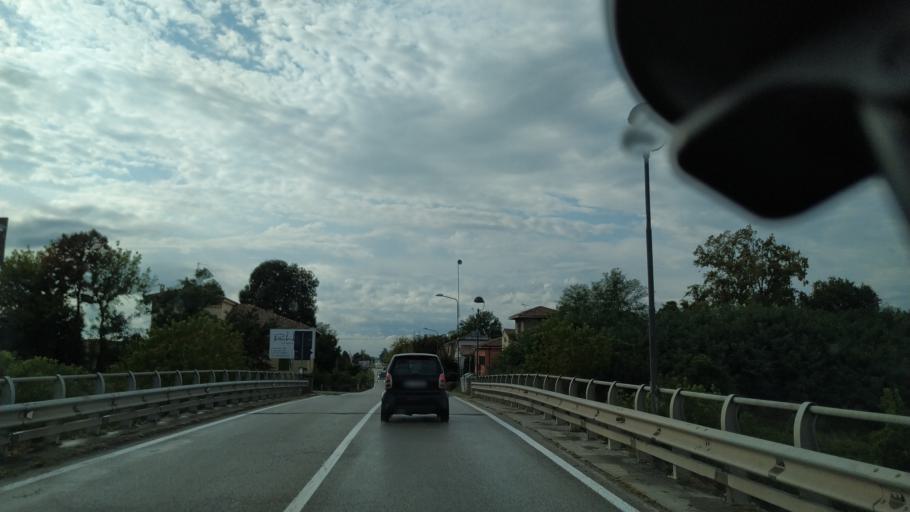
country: IT
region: Emilia-Romagna
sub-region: Provincia di Ferrara
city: Sant'Agostino
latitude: 44.7942
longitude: 11.3808
